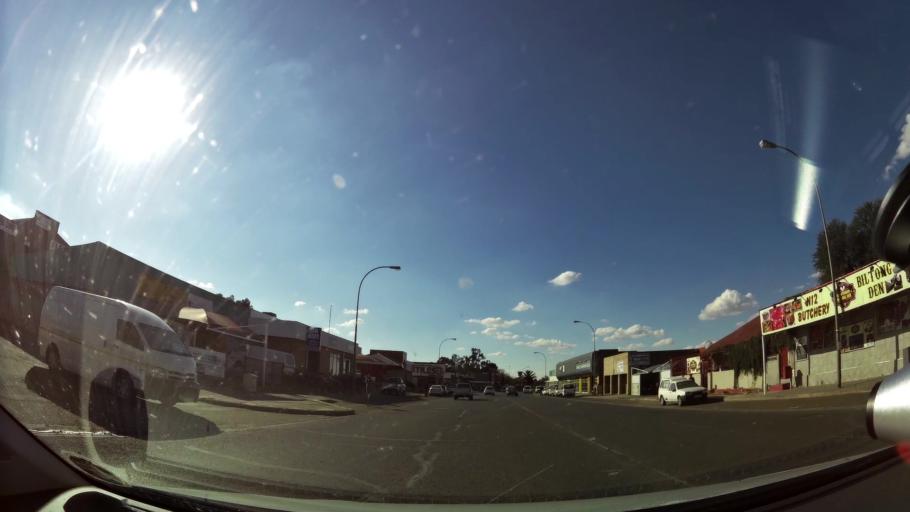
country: ZA
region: Northern Cape
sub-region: Frances Baard District Municipality
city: Kimberley
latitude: -28.7327
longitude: 24.7640
